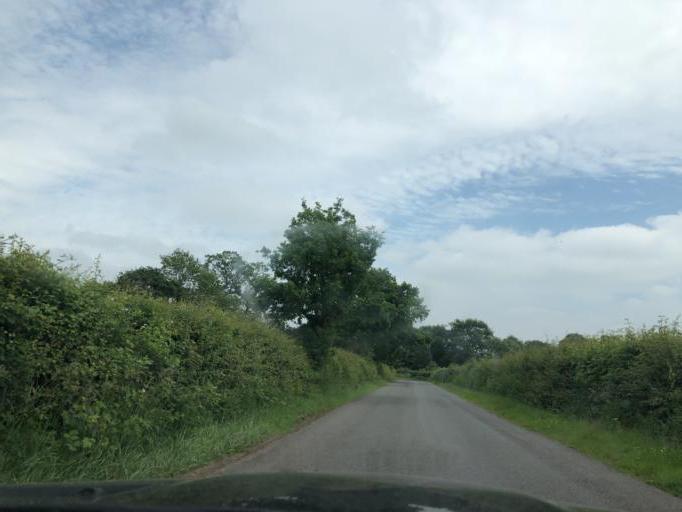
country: GB
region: England
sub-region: Warwickshire
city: Wroxall
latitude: 52.3321
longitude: -1.6366
